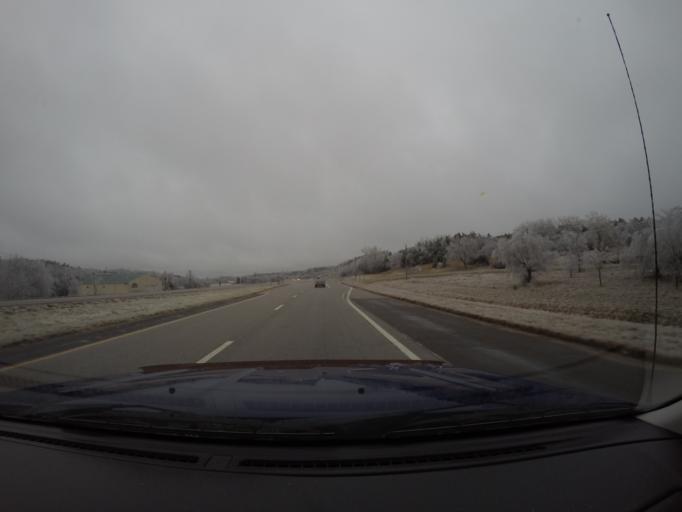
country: US
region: Kansas
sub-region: Riley County
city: Manhattan
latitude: 39.1544
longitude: -96.5384
